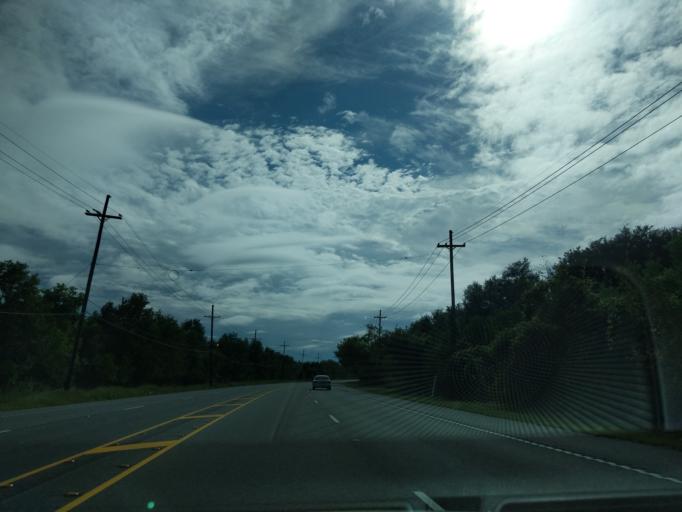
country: US
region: Louisiana
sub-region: Saint Bernard Parish
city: Meraux
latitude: 30.0631
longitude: -89.8655
